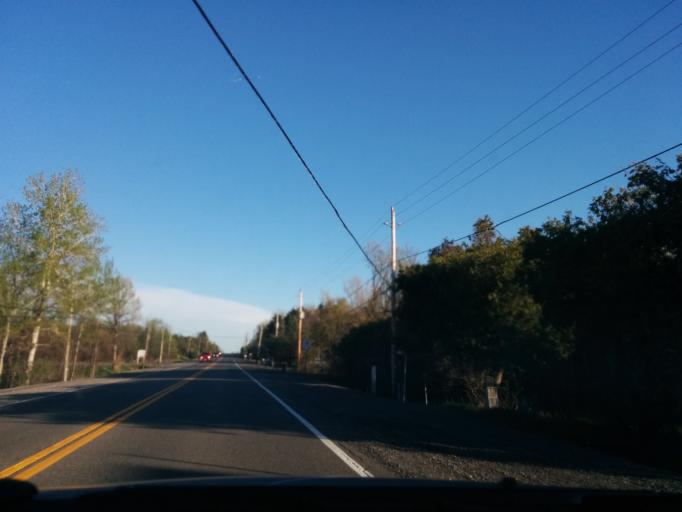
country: CA
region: Ontario
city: Ottawa
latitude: 45.1985
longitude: -75.6372
